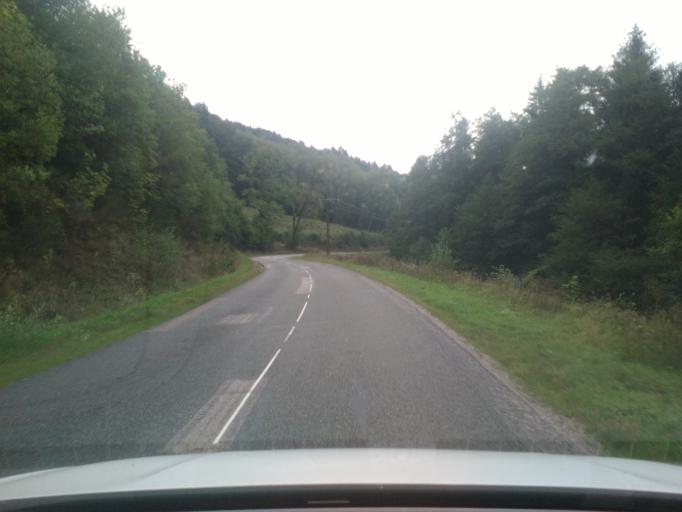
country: FR
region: Lorraine
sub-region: Departement des Vosges
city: Senones
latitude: 48.3412
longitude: 6.9801
